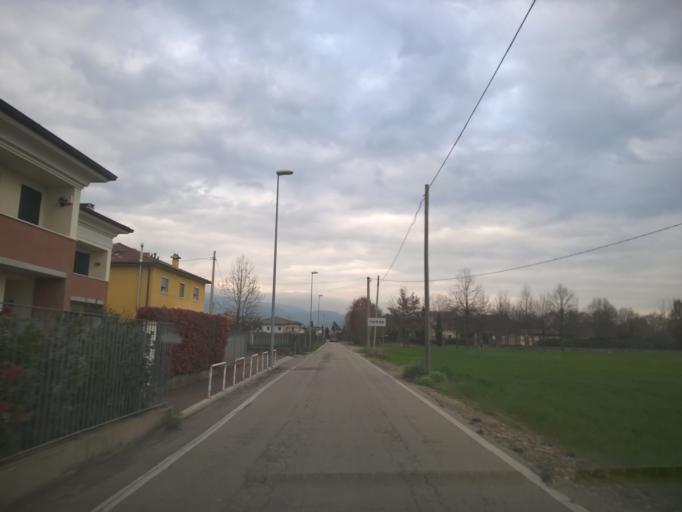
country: IT
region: Veneto
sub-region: Provincia di Vicenza
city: Thiene
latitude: 45.6952
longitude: 11.4729
